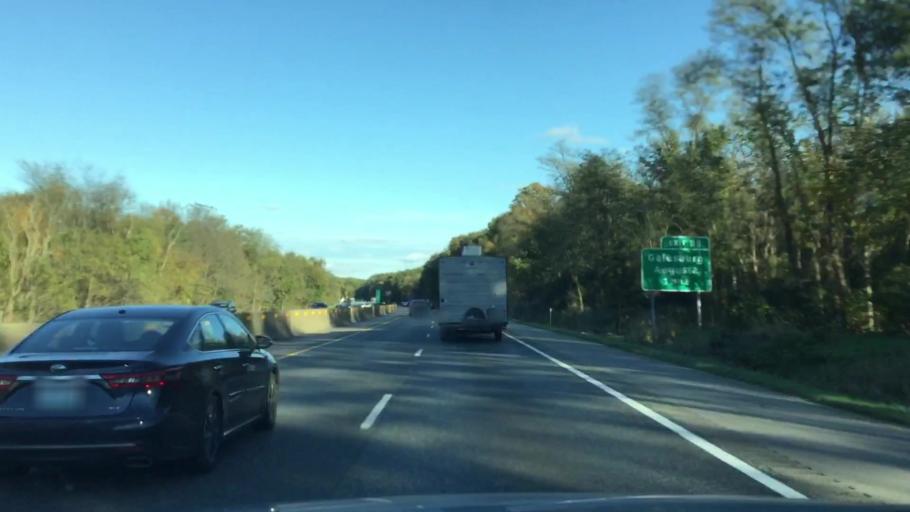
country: US
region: Michigan
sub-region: Kalamazoo County
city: Galesburg
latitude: 42.2693
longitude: -85.4547
